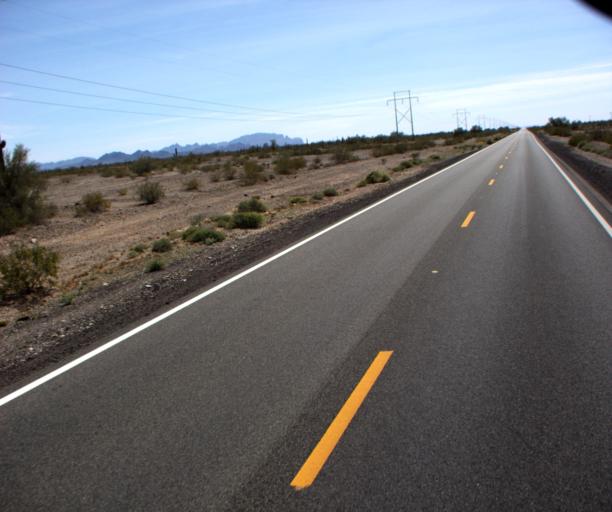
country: US
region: Arizona
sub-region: La Paz County
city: Quartzsite
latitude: 33.6141
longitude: -114.2171
